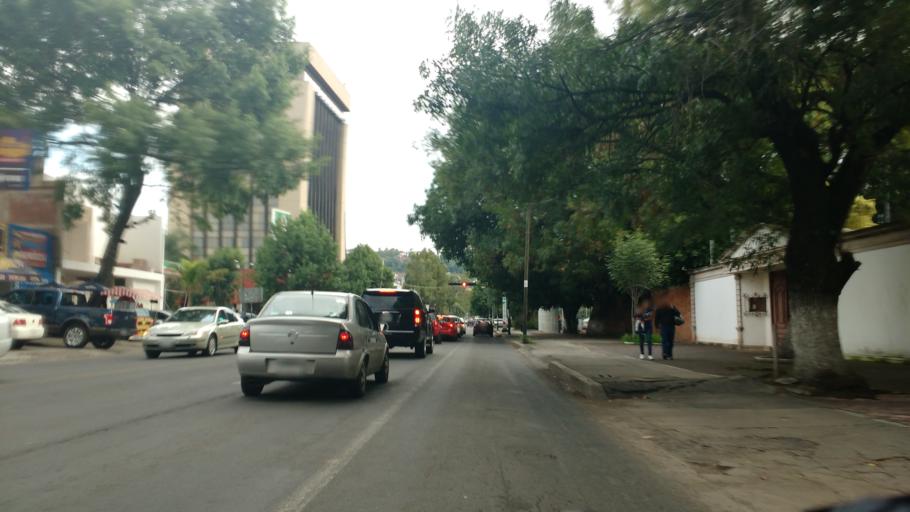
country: MX
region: Michoacan
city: Morelia
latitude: 19.6915
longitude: -101.1796
